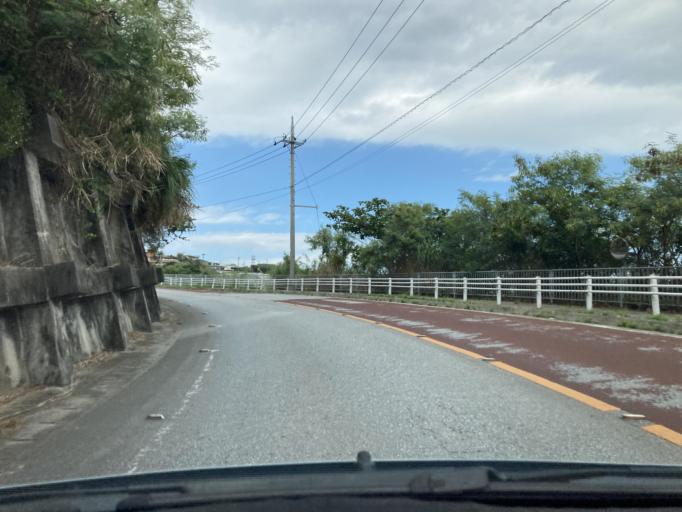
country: JP
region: Okinawa
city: Ginowan
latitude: 26.2657
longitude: 127.7860
